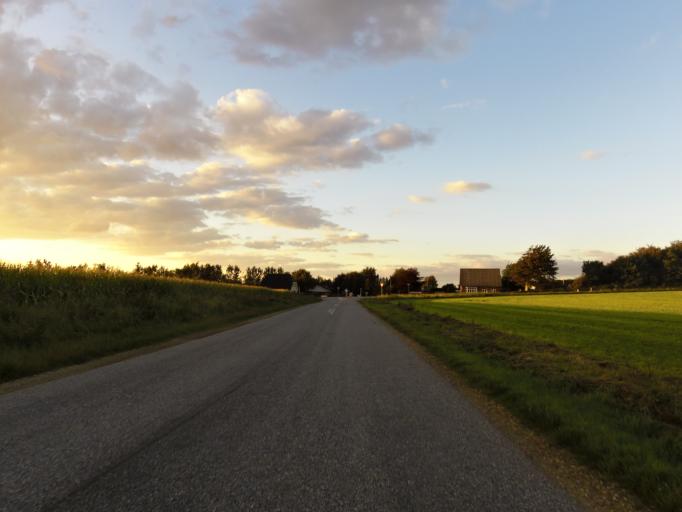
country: DK
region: South Denmark
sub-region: Haderslev Kommune
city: Gram
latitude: 55.2533
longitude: 8.9060
